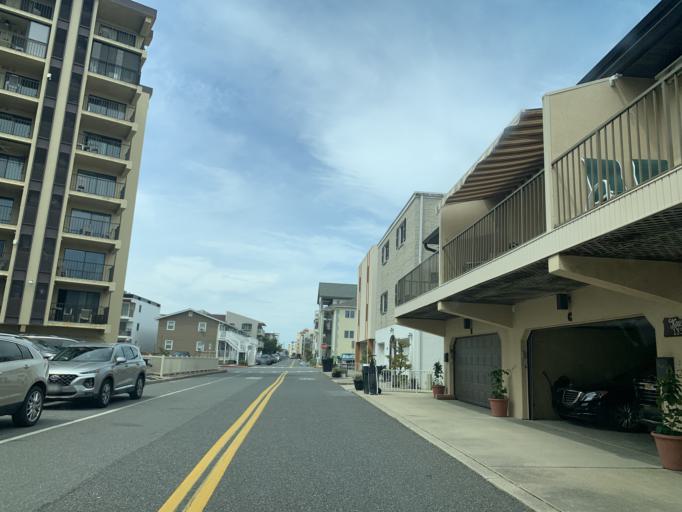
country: US
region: Delaware
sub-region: Sussex County
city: Bethany Beach
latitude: 38.4407
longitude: -75.0515
